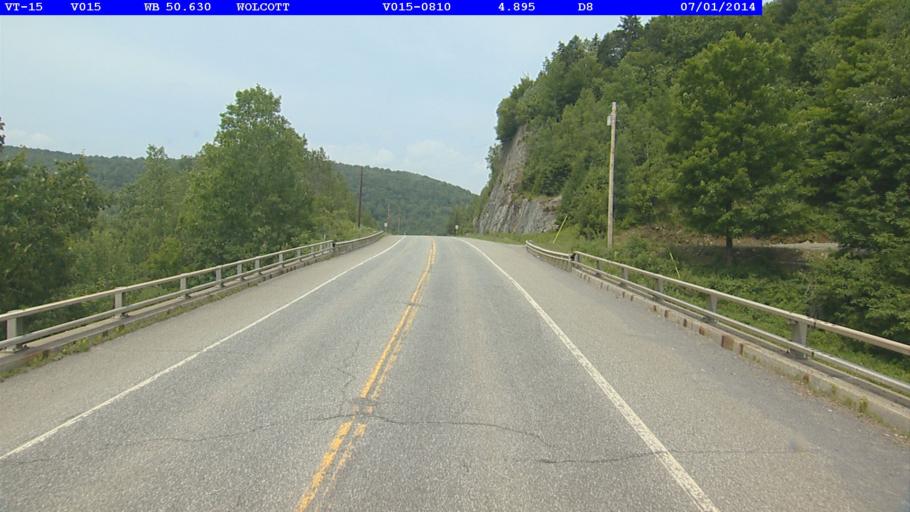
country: US
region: Vermont
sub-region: Caledonia County
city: Hardwick
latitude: 44.5403
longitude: -72.4518
